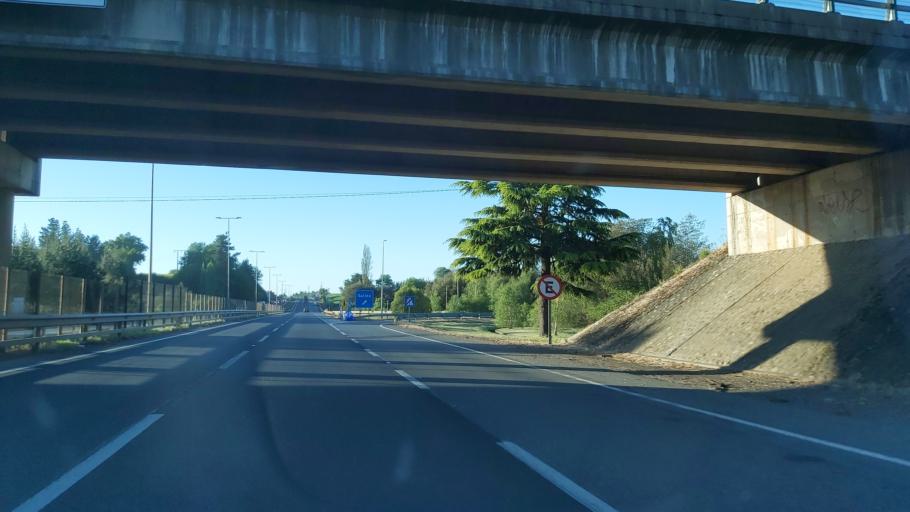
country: CL
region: Araucania
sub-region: Provincia de Malleco
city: Collipulli
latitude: -38.0656
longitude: -72.3800
